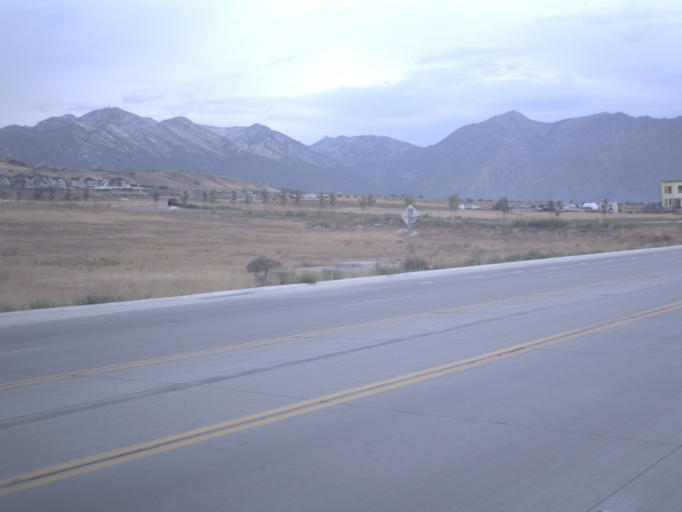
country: US
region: Utah
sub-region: Utah County
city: Lehi
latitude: 40.4326
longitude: -111.8623
